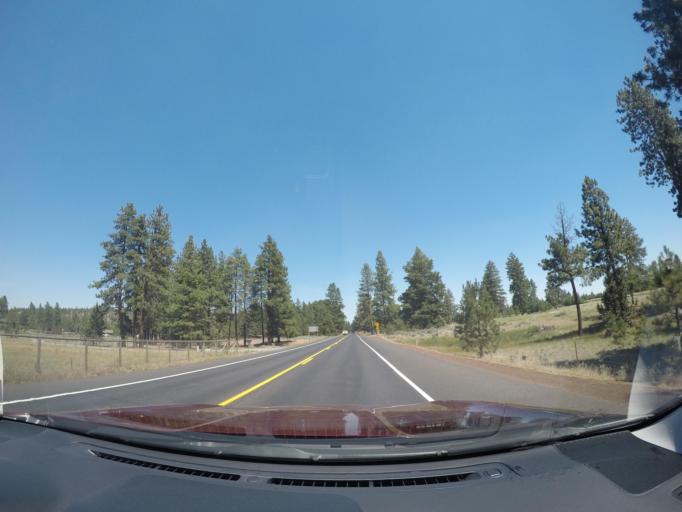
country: US
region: Oregon
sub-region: Deschutes County
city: Sisters
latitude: 44.2878
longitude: -121.5331
